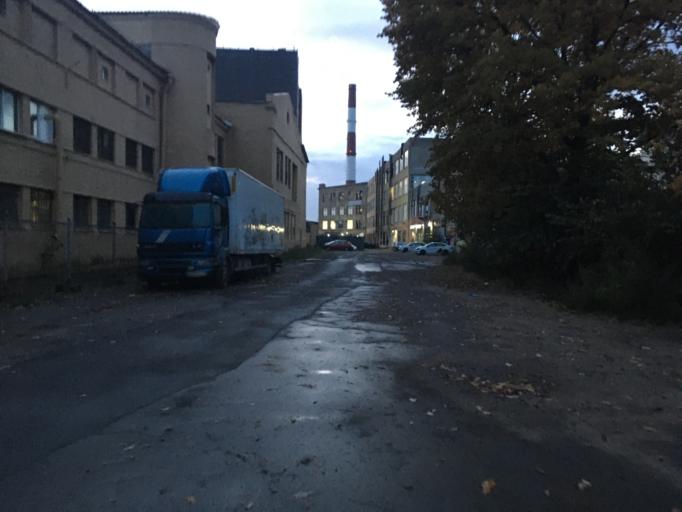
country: RU
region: St.-Petersburg
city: Centralniy
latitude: 59.9065
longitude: 30.3429
